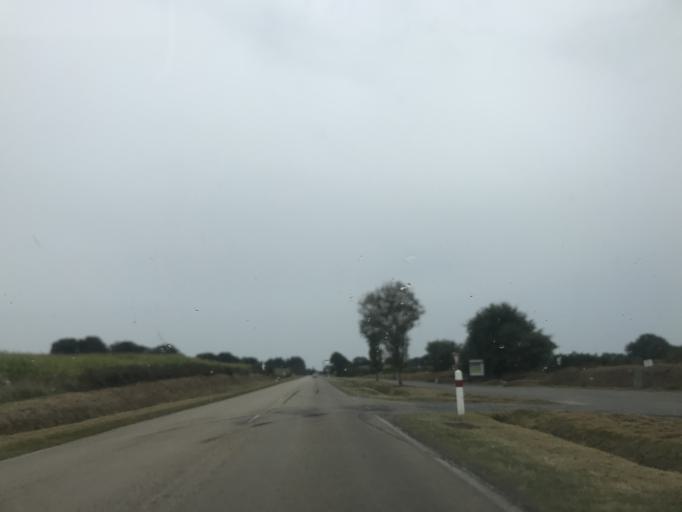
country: FR
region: Brittany
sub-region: Departement du Finistere
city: Plouneour-Menez
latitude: 48.4555
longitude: -3.8778
